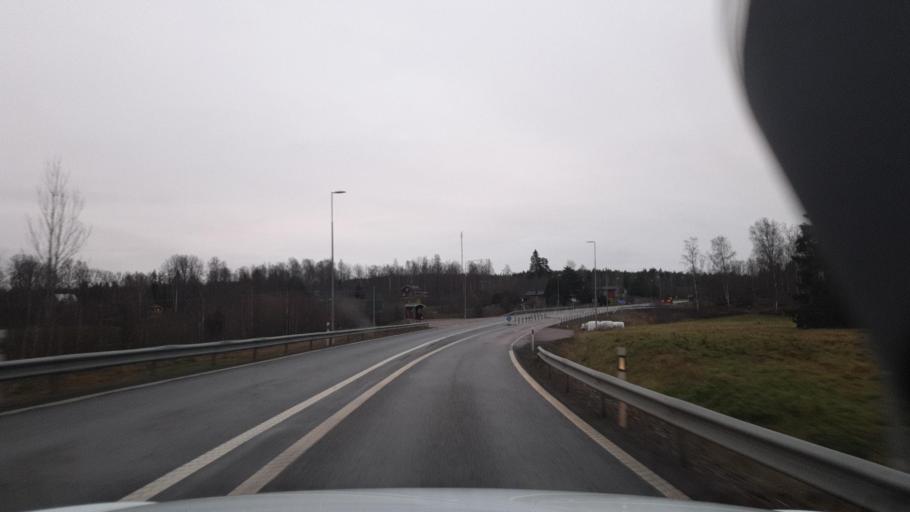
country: SE
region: Vaermland
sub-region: Eda Kommun
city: Amotfors
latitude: 59.7598
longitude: 12.4393
